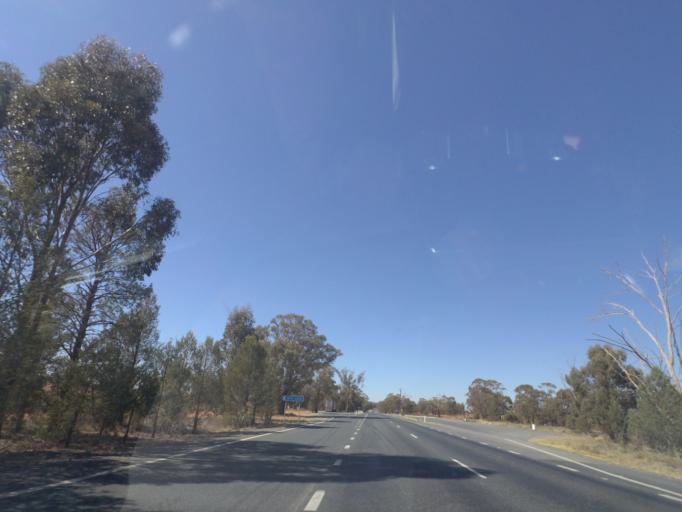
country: AU
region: New South Wales
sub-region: Bland
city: West Wyalong
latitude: -34.1983
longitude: 147.1106
